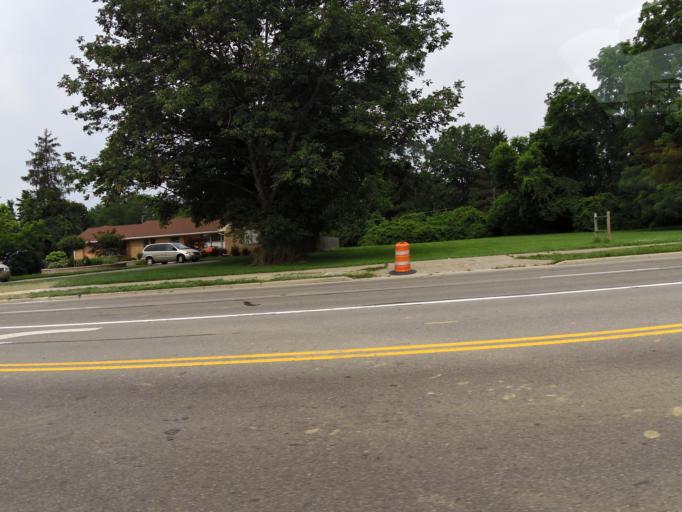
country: US
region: Ohio
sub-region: Greene County
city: Bellbrook
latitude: 39.6628
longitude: -84.1091
